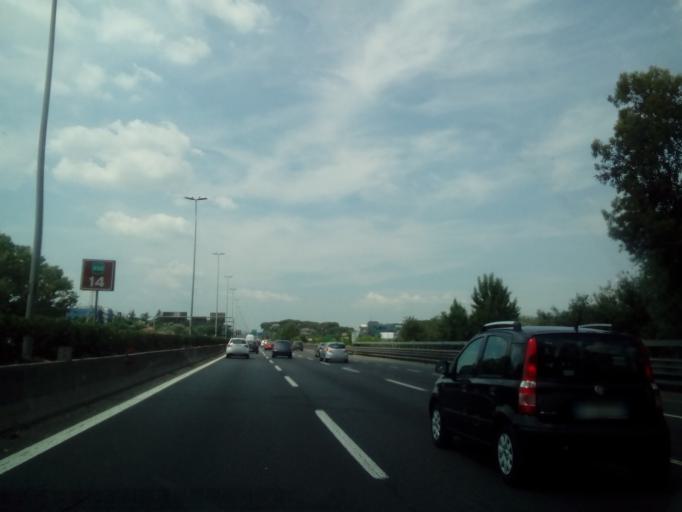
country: IT
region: Latium
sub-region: Citta metropolitana di Roma Capitale
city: Setteville
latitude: 41.9239
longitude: 12.6089
